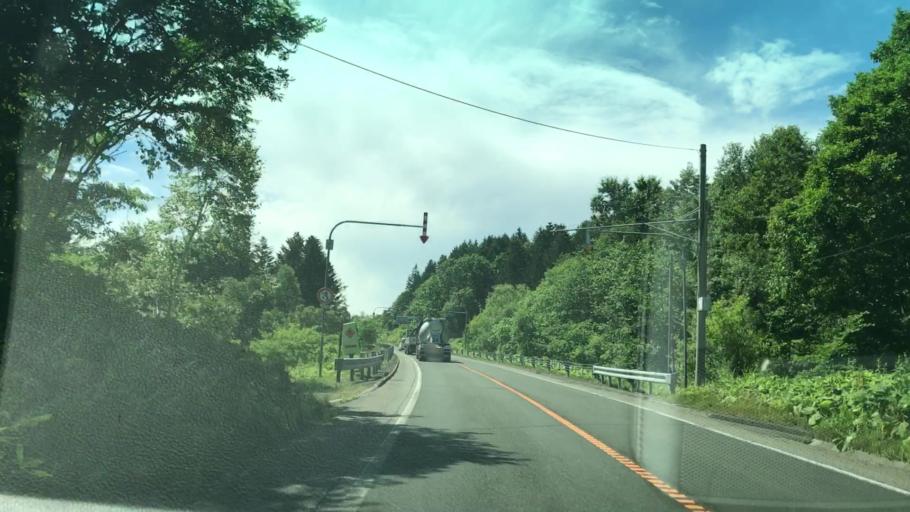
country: JP
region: Hokkaido
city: Shimo-furano
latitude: 42.9166
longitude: 142.4471
